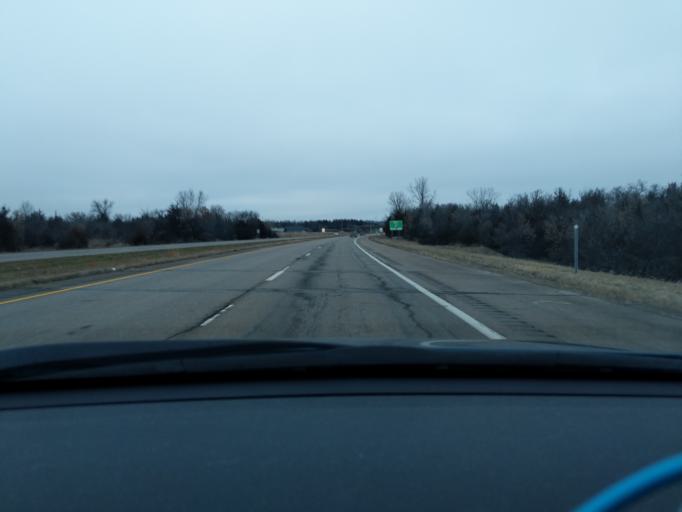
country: US
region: Minnesota
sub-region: Yellow Medicine County
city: Granite Falls
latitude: 44.7977
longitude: -95.5482
